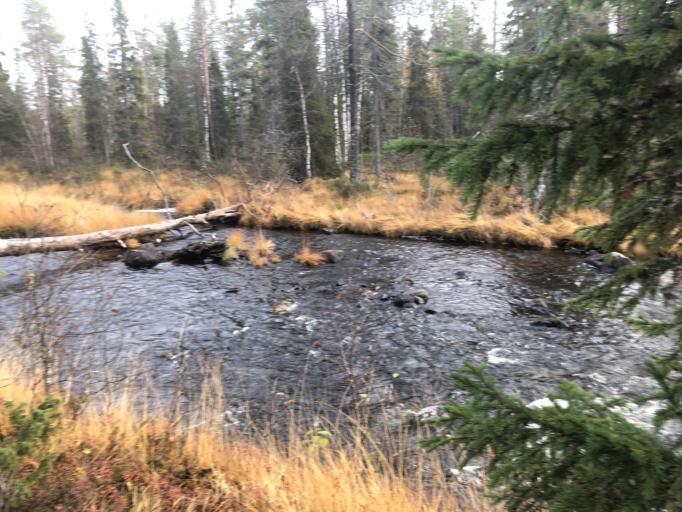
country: FI
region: Northern Ostrobothnia
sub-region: Koillismaa
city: Kuusamo
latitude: 66.5037
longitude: 29.3523
